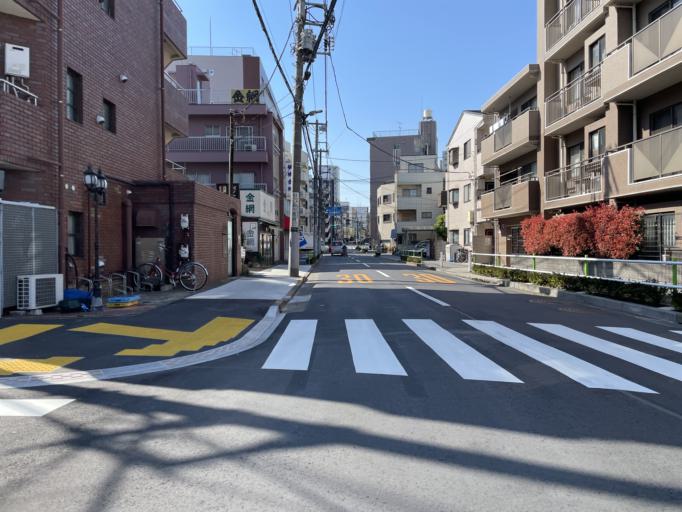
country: JP
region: Saitama
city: Kawaguchi
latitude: 35.7556
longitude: 139.6910
